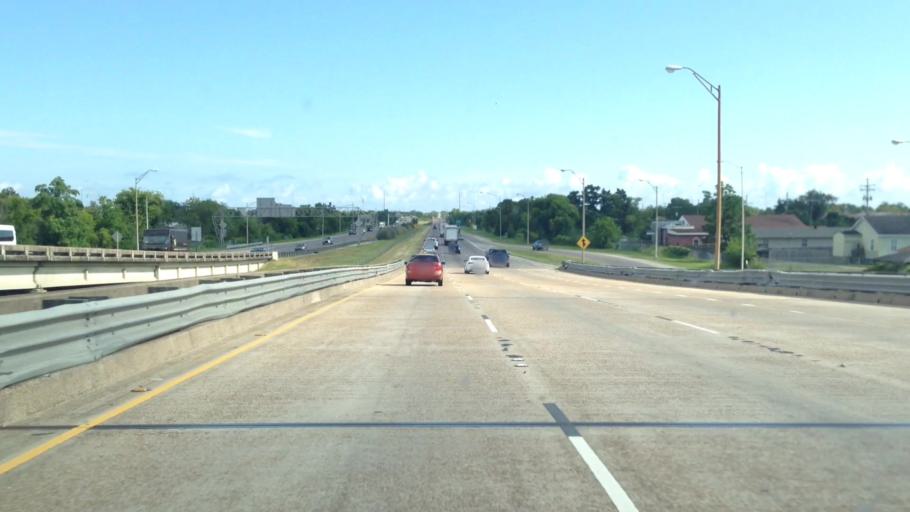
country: US
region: Louisiana
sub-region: Saint Bernard Parish
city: Arabi
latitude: 30.0115
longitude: -90.0129
